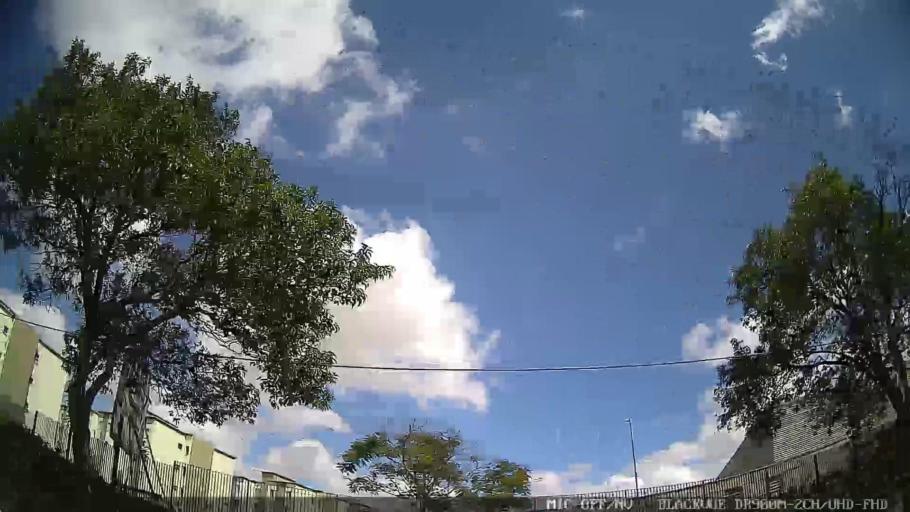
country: BR
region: Sao Paulo
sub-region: Diadema
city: Diadema
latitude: -23.6548
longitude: -46.5936
